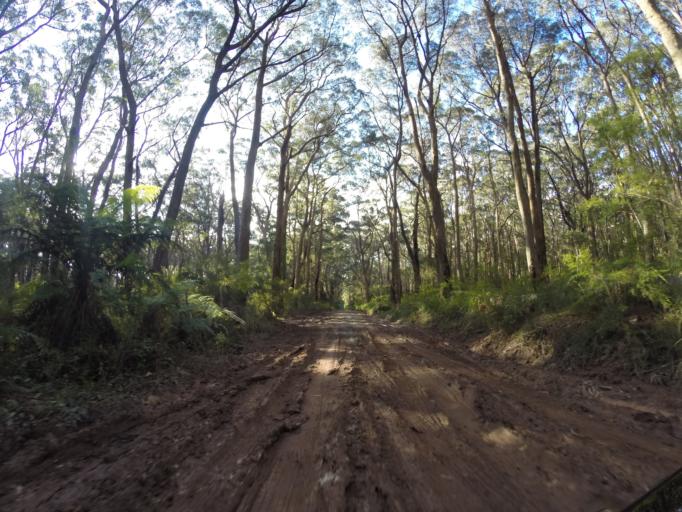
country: AU
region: New South Wales
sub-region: Wollongong
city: Cordeaux Heights
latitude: -34.4087
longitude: 150.7855
